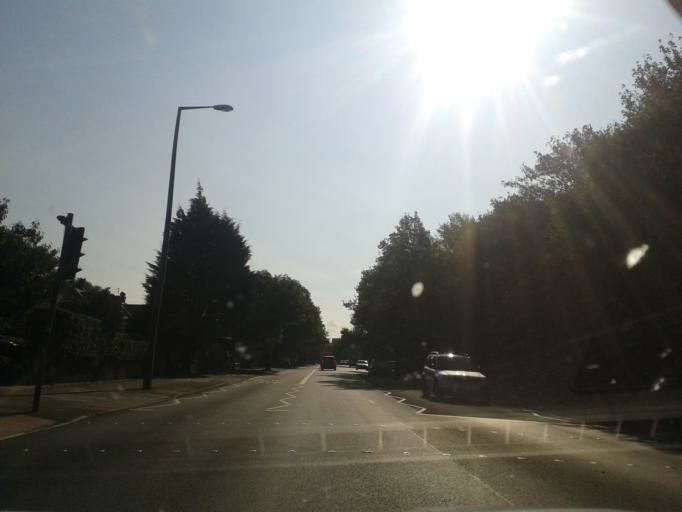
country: GB
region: England
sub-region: Lancashire
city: Lancaster
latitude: 54.0587
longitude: -2.8227
